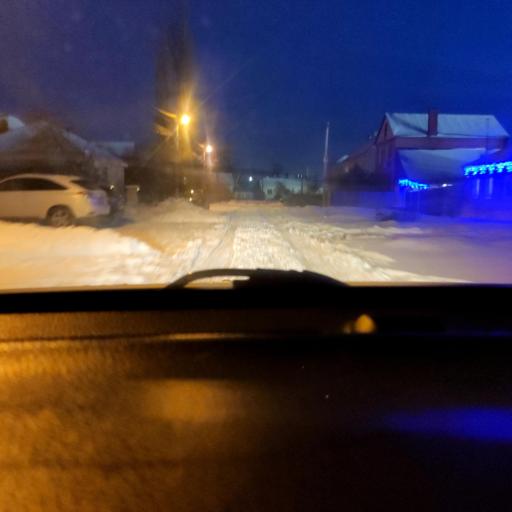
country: RU
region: Voronezj
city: Voronezh
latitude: 51.7346
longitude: 39.2618
